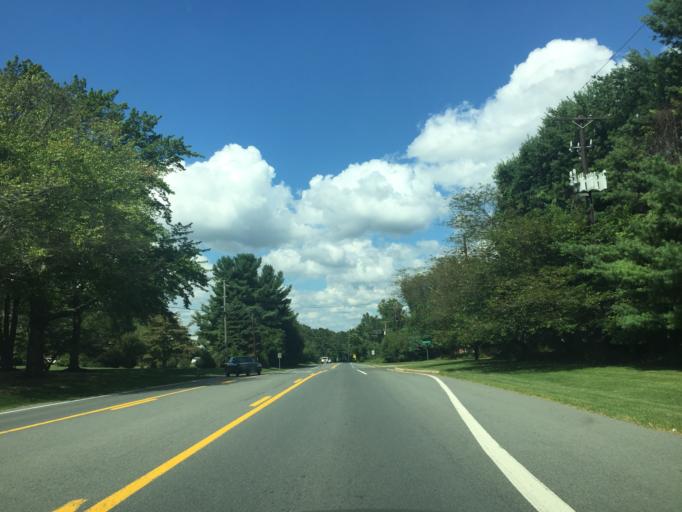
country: US
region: Maryland
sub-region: Montgomery County
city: Rossmoor
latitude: 39.1142
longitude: -77.0937
